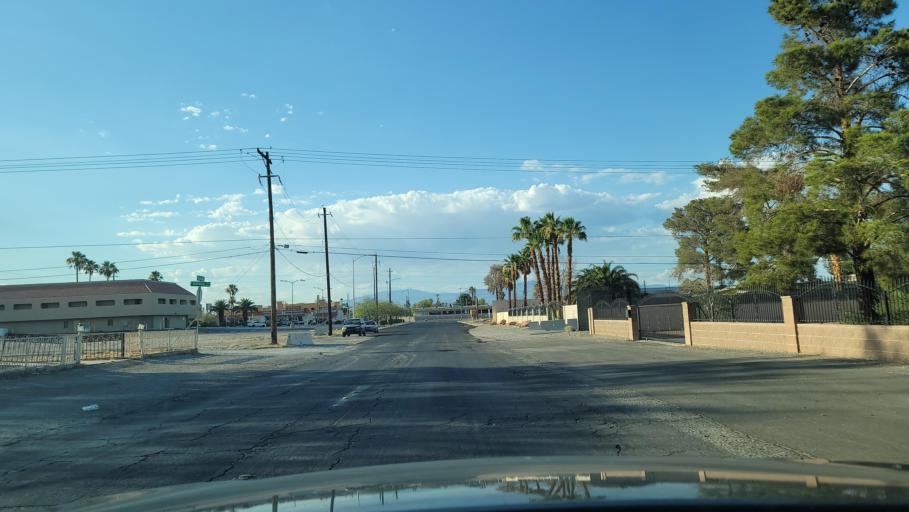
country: US
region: Nevada
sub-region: Clark County
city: Spring Valley
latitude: 36.1570
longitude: -115.2191
